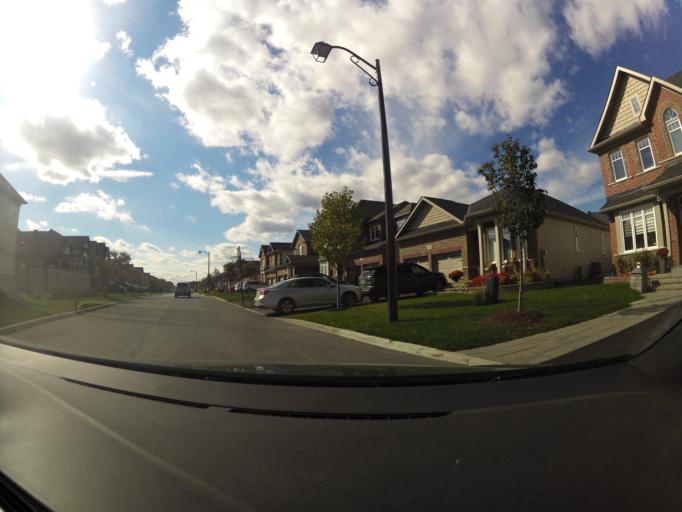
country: CA
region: Ontario
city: Bells Corners
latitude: 45.2758
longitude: -75.8880
